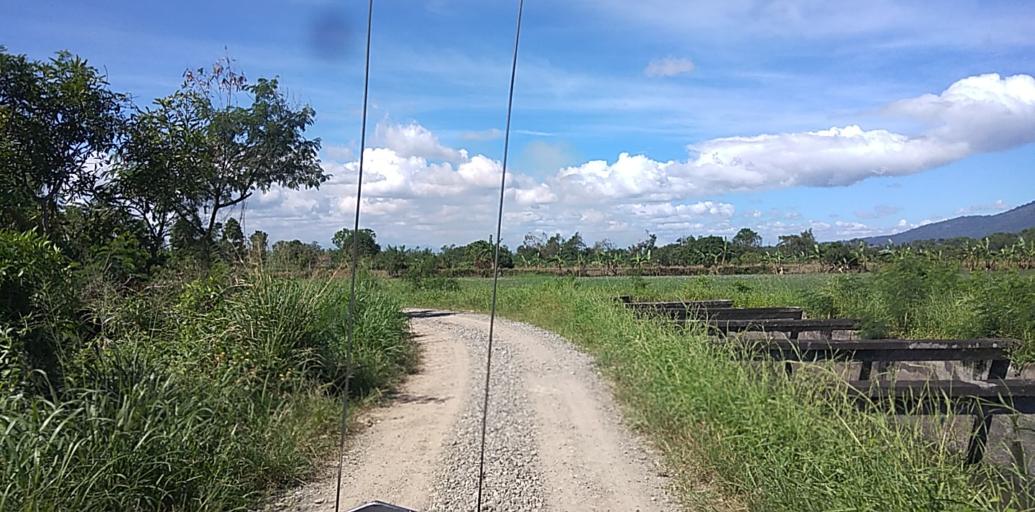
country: PH
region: Central Luzon
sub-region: Province of Pampanga
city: Arayat
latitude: 15.1291
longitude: 120.7884
